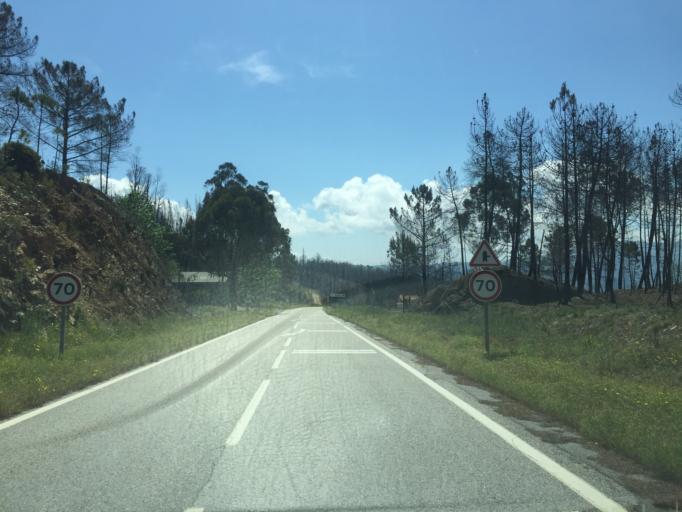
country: PT
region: Coimbra
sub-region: Pampilhosa da Serra
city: Pampilhosa da Serra
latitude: 40.0064
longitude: -7.9803
